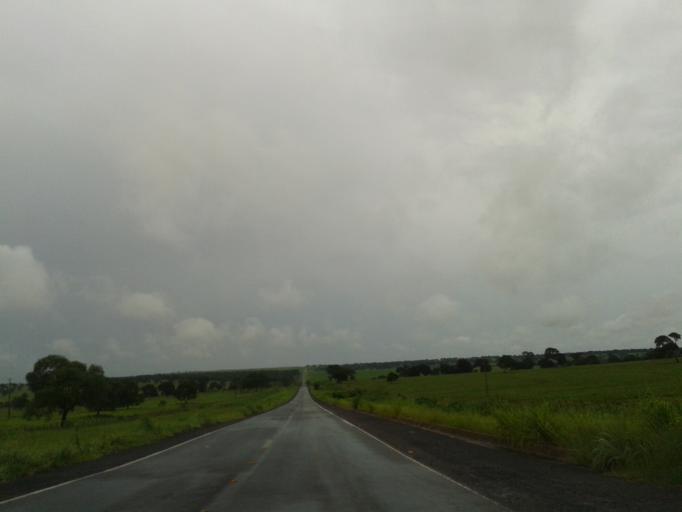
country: BR
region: Minas Gerais
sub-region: Santa Vitoria
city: Santa Vitoria
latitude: -19.1532
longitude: -50.1408
